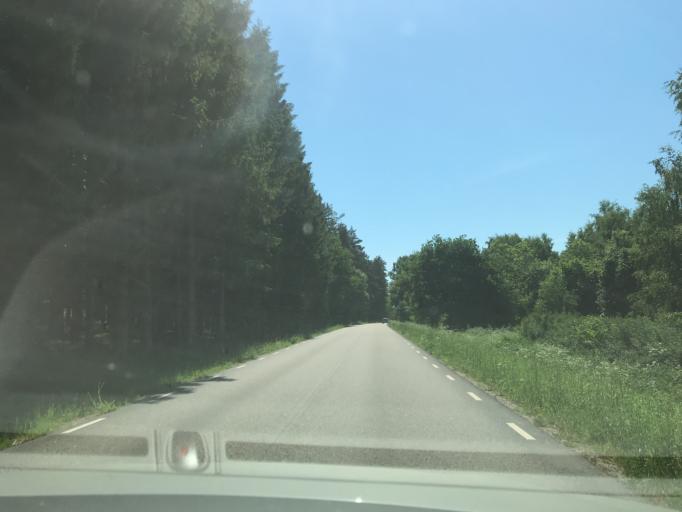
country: SE
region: Vaestra Goetaland
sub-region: Gotene Kommun
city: Kallby
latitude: 58.5295
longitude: 13.3241
